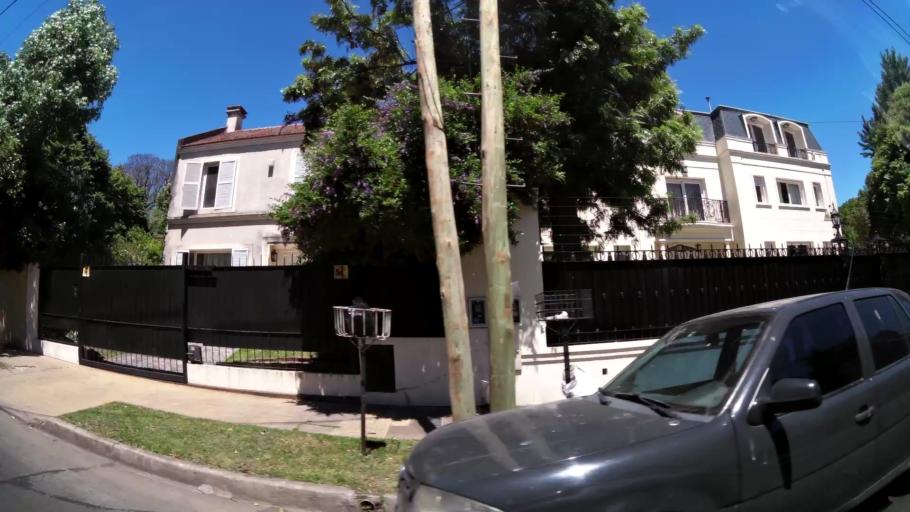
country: AR
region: Buenos Aires
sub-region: Partido de San Isidro
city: San Isidro
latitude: -34.4578
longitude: -58.5201
